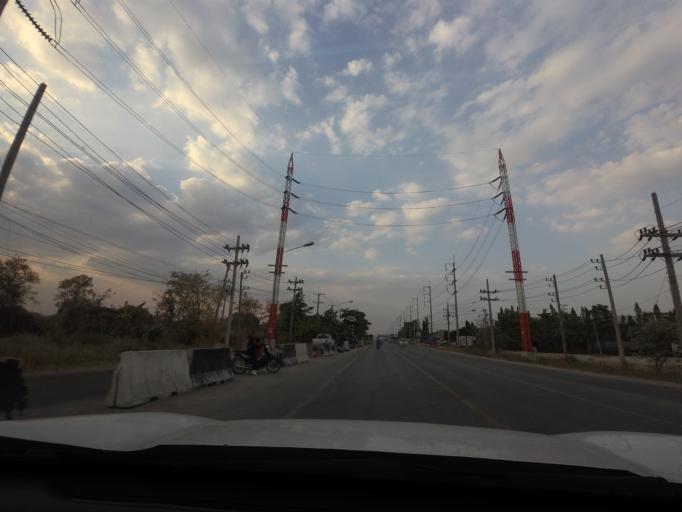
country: TH
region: Nakhon Ratchasima
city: Pak Chong
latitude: 14.6766
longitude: 101.4544
